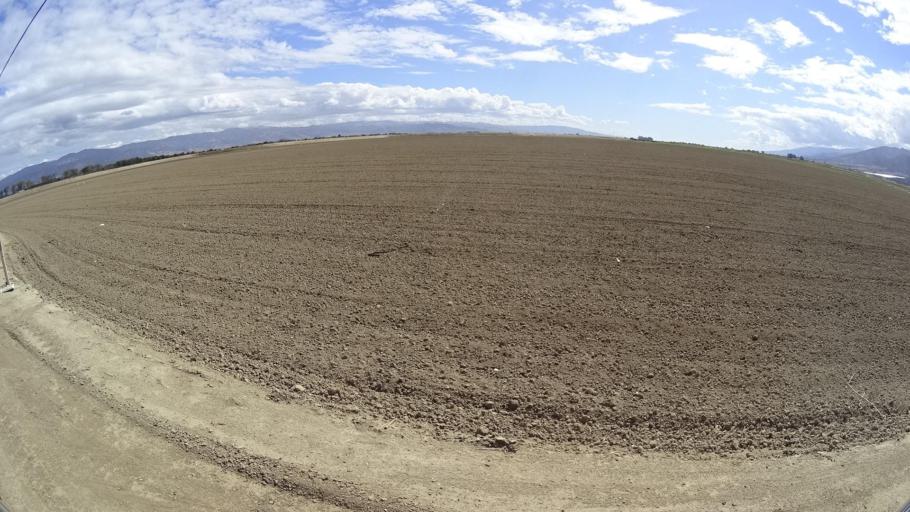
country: US
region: California
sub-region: Monterey County
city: Chualar
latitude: 36.6052
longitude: -121.6007
